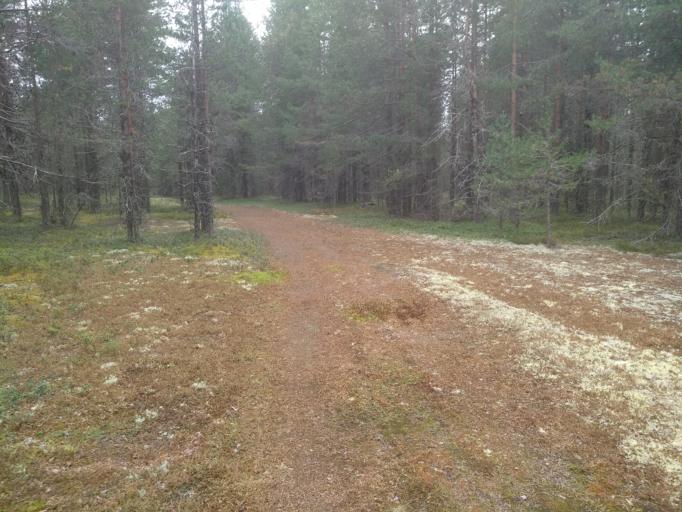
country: RU
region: Republic of Karelia
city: Kostomuksha
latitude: 64.9794
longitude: 30.6936
